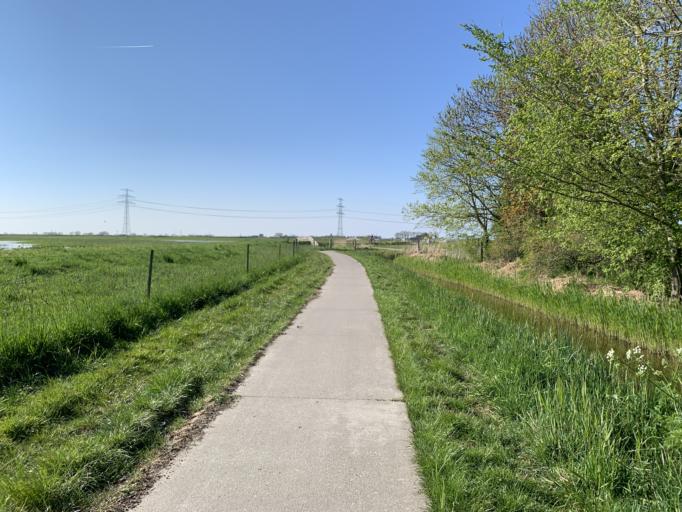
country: NL
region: Groningen
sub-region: Gemeente Winsum
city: Winsum
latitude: 53.2879
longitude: 6.5146
